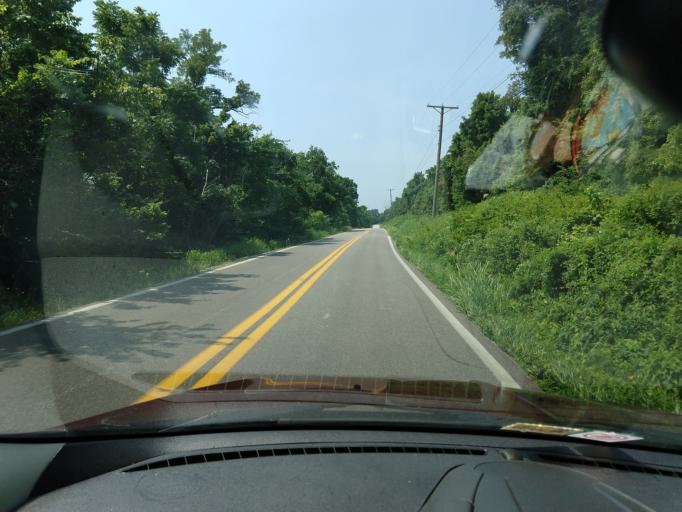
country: US
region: West Virginia
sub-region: Mason County
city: New Haven
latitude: 38.9195
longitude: -81.9152
